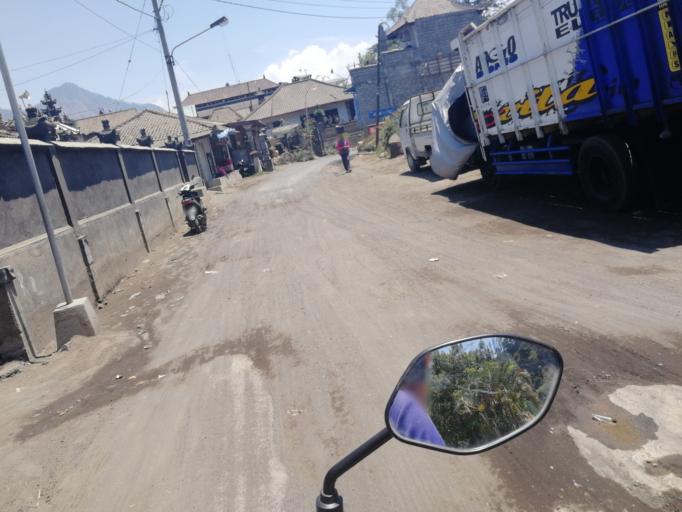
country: ID
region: Bali
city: Banjar Trunyan
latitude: -8.2243
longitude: 115.4095
